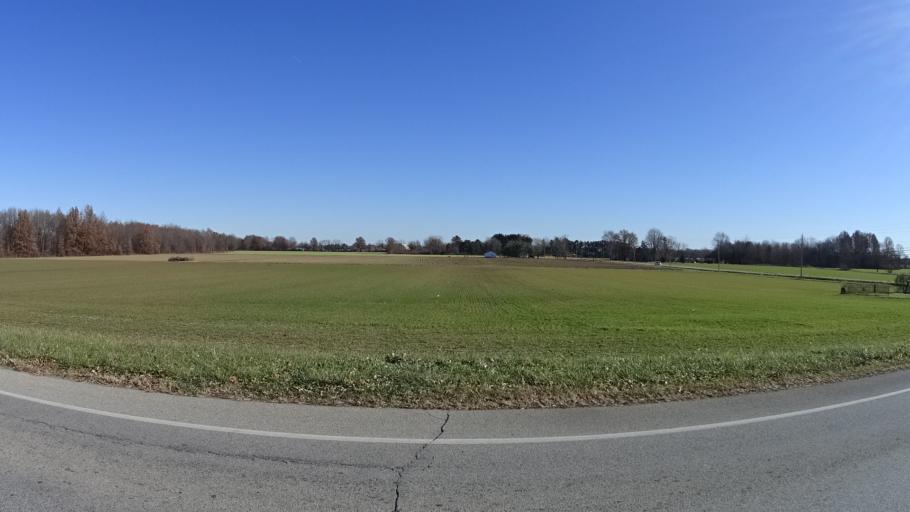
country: US
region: Ohio
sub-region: Lorain County
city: Elyria
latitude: 41.3374
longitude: -82.1515
